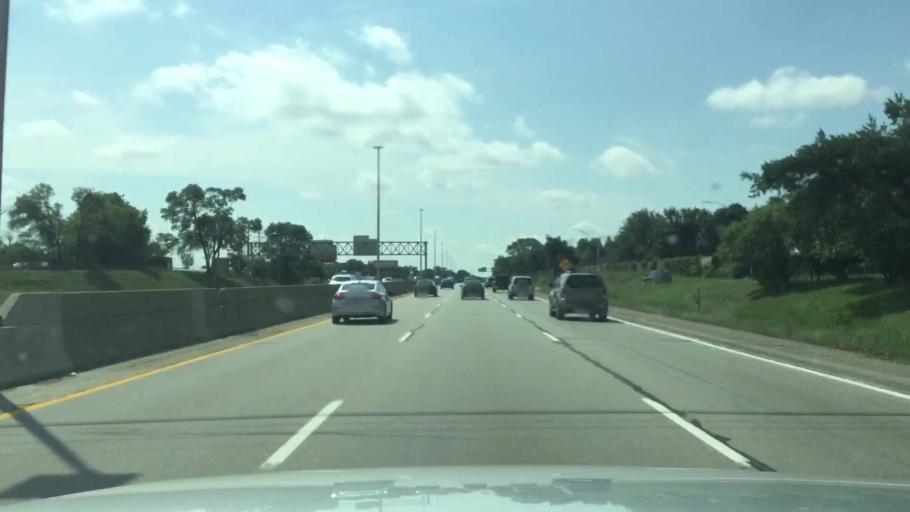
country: US
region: Michigan
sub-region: Kent County
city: Wyoming
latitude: 42.8984
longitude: -85.6783
